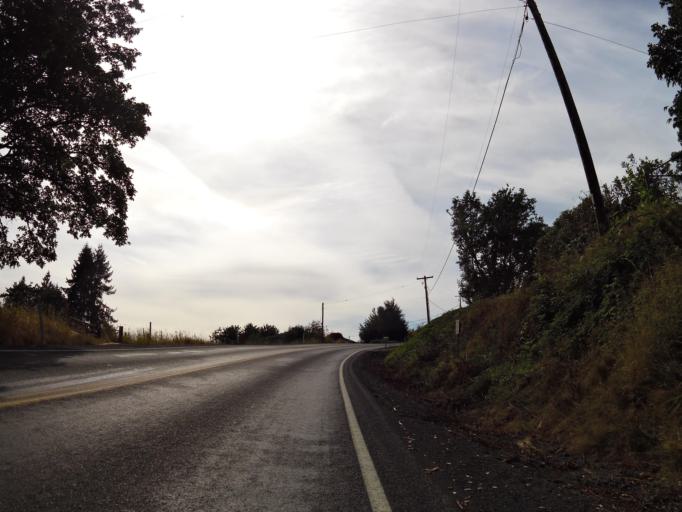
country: US
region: Washington
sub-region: Lewis County
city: Chehalis
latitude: 46.6275
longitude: -122.9675
